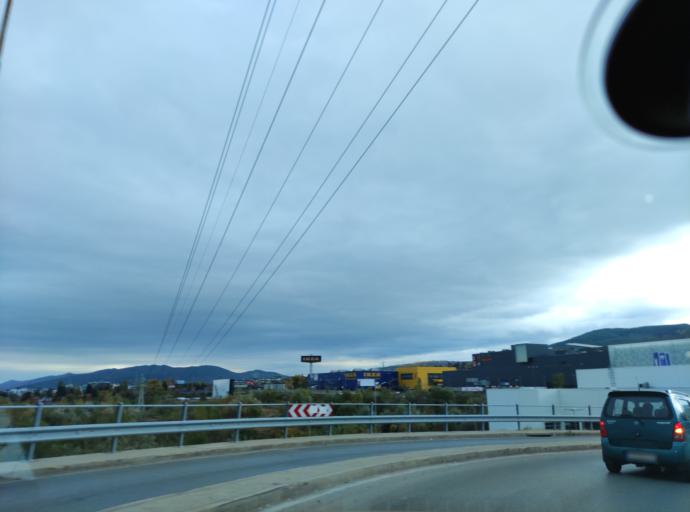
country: BG
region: Sofia-Capital
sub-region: Stolichna Obshtina
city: Sofia
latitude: 42.6271
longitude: 23.3522
